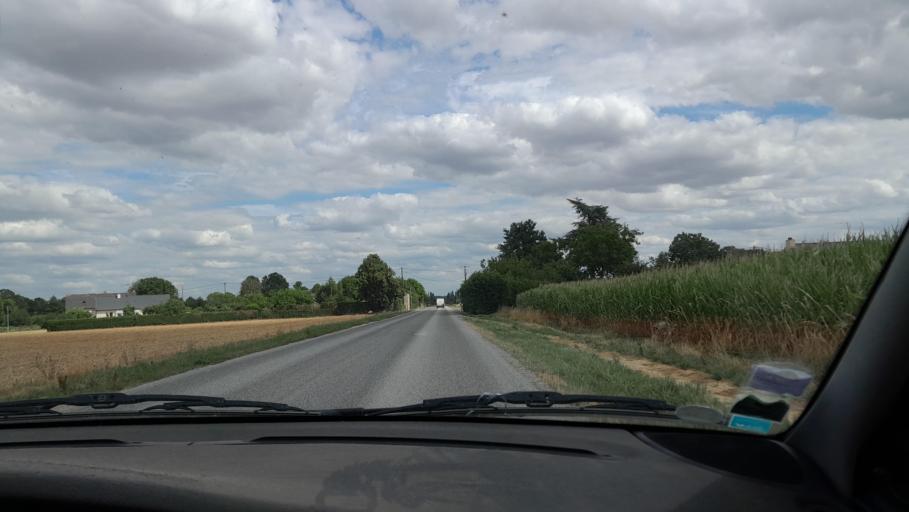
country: FR
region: Pays de la Loire
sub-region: Departement de la Mayenne
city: Craon
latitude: 47.8634
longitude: -0.9844
